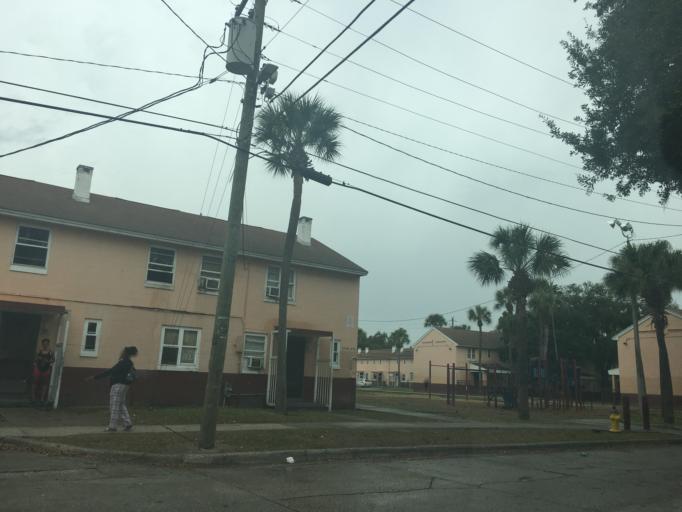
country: US
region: Florida
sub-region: Hillsborough County
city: Tampa
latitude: 27.9788
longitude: -82.4566
